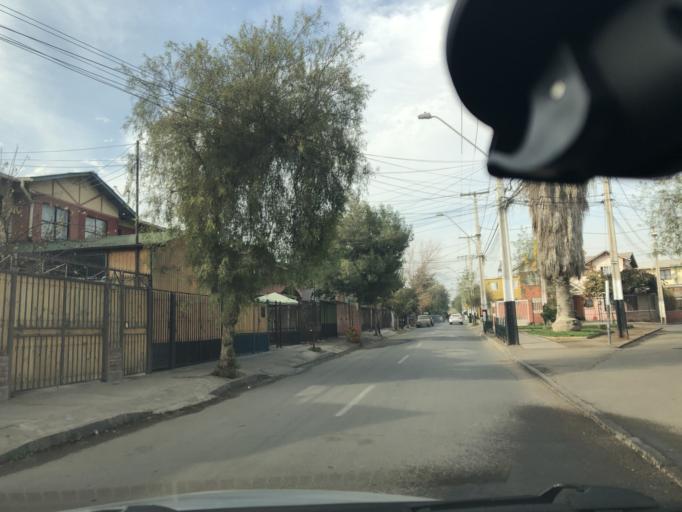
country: CL
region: Santiago Metropolitan
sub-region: Provincia de Cordillera
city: Puente Alto
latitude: -33.5815
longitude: -70.5524
